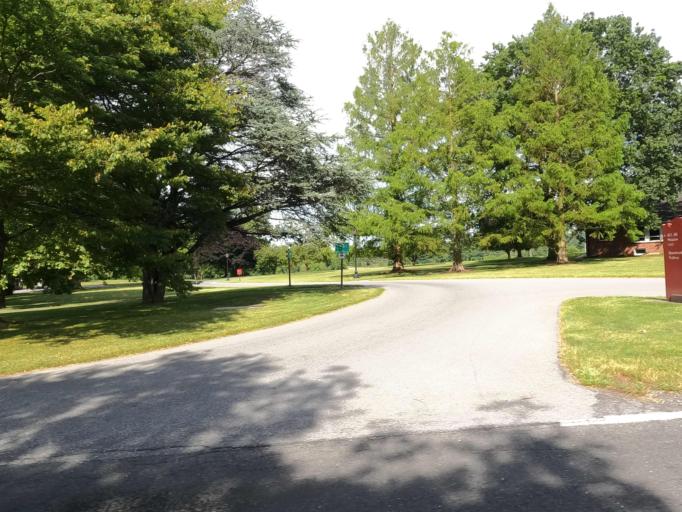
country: US
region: Pennsylvania
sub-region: Dauphin County
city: Palmdale
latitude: 40.2650
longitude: -76.6172
